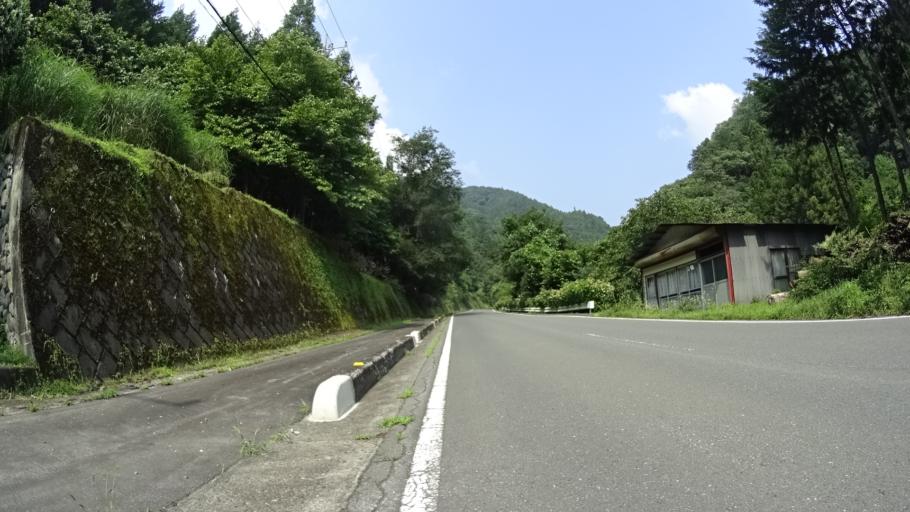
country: JP
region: Gunma
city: Tomioka
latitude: 36.0534
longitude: 138.8642
